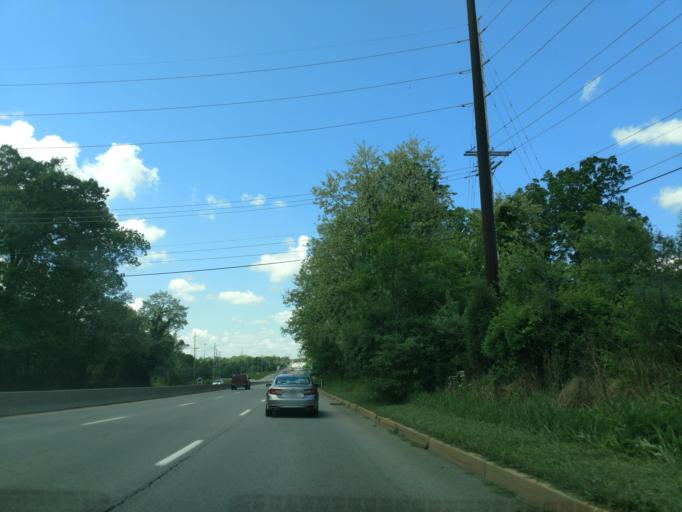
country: US
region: Pennsylvania
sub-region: Chester County
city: Exton
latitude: 40.0593
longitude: -75.6651
